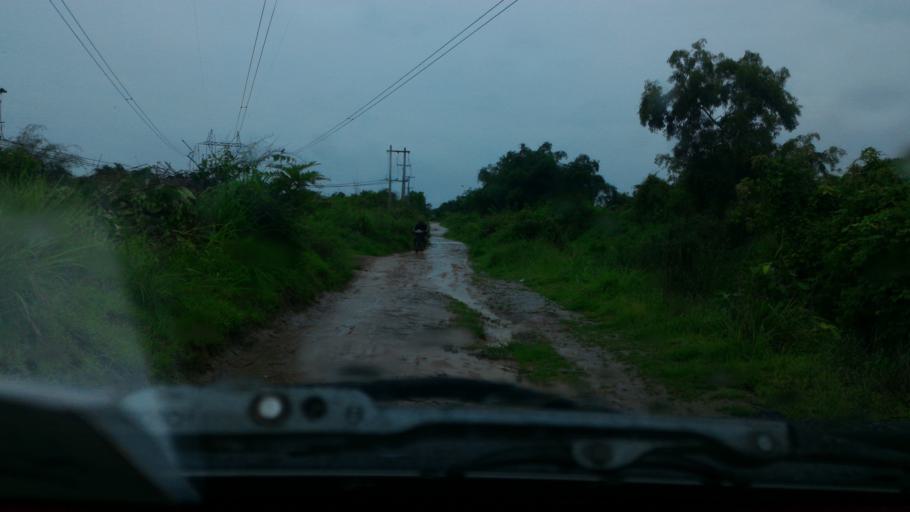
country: MM
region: Bago
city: Thanatpin
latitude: 17.2107
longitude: 95.9745
